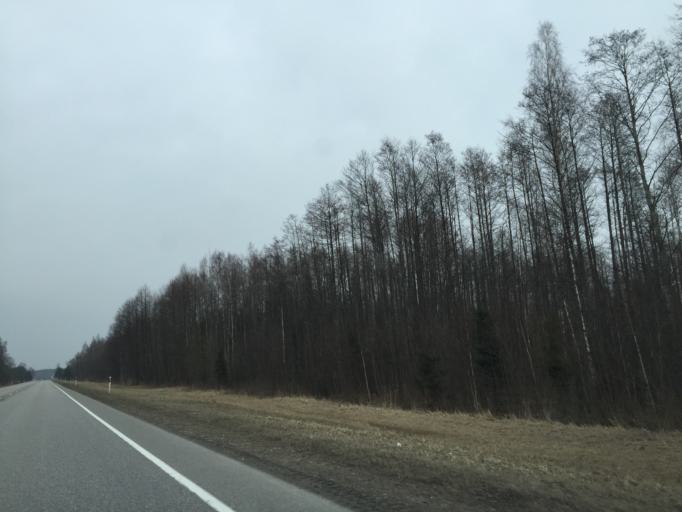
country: LV
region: Salacgrivas
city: Ainazi
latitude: 58.0661
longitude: 24.5114
